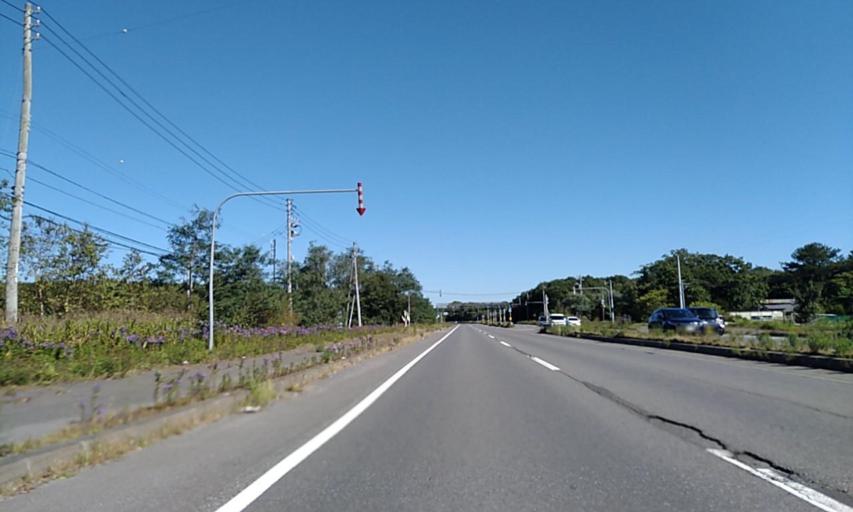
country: JP
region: Hokkaido
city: Chitose
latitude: 42.7184
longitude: 141.7082
